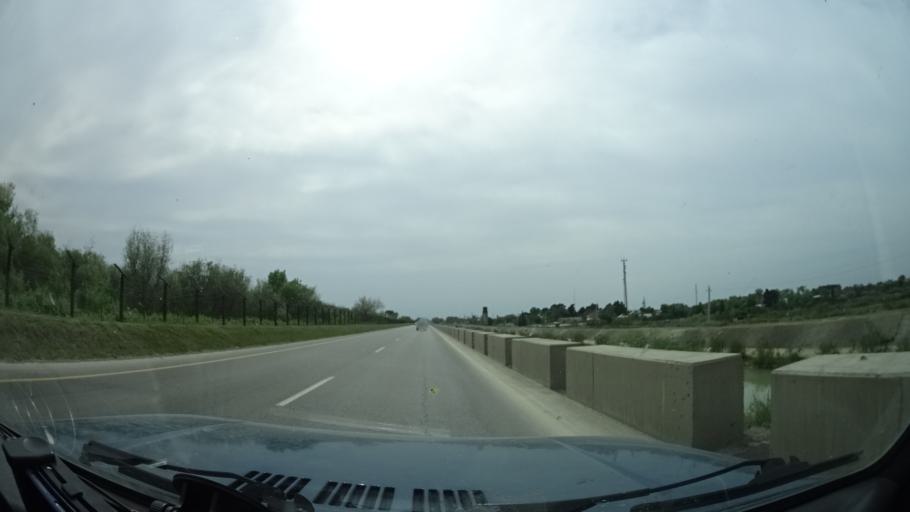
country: IR
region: Ardabil
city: Parsabad
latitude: 39.7375
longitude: 47.9652
